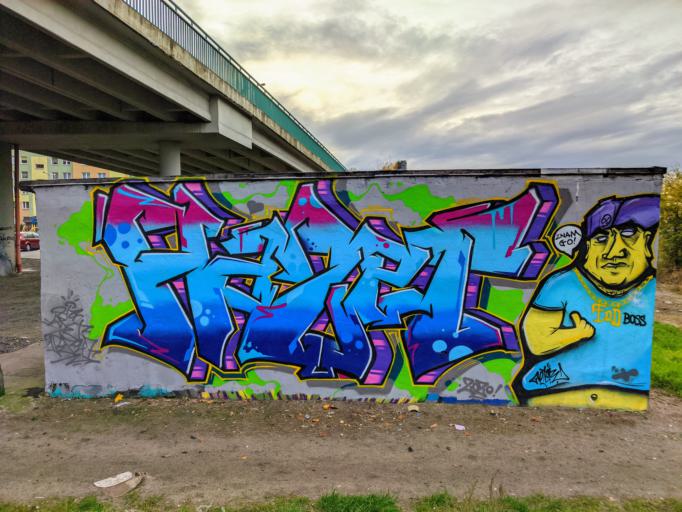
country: PL
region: Lubusz
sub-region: Powiat nowosolski
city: Nowa Sol
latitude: 51.8086
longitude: 15.7022
